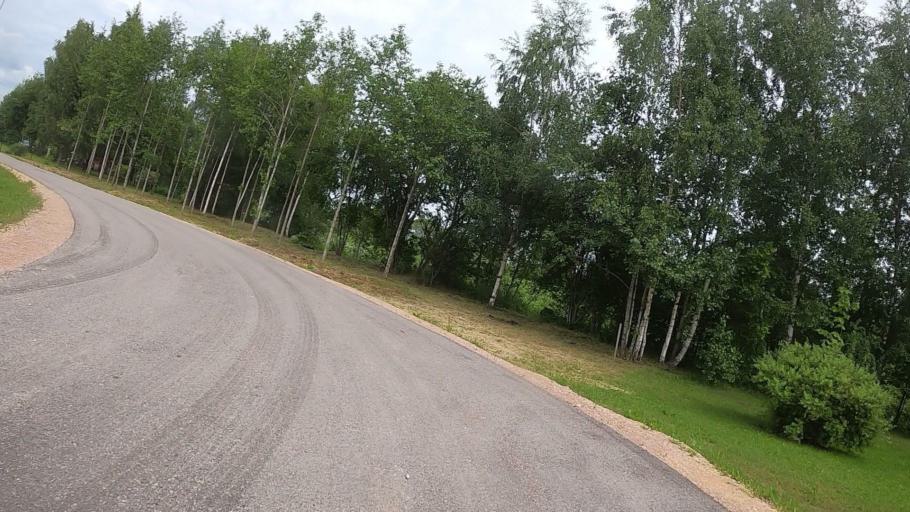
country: LV
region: Olaine
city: Olaine
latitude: 56.7748
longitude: 23.9231
